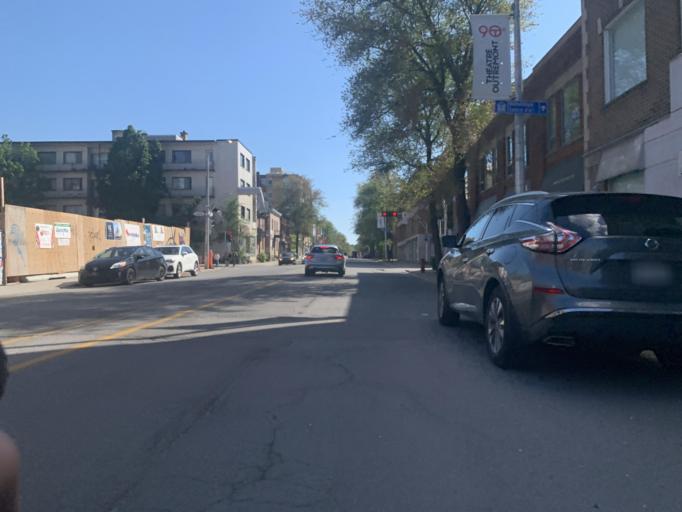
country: CA
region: Quebec
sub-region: Montreal
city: Montreal
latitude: 45.5242
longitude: -73.6117
